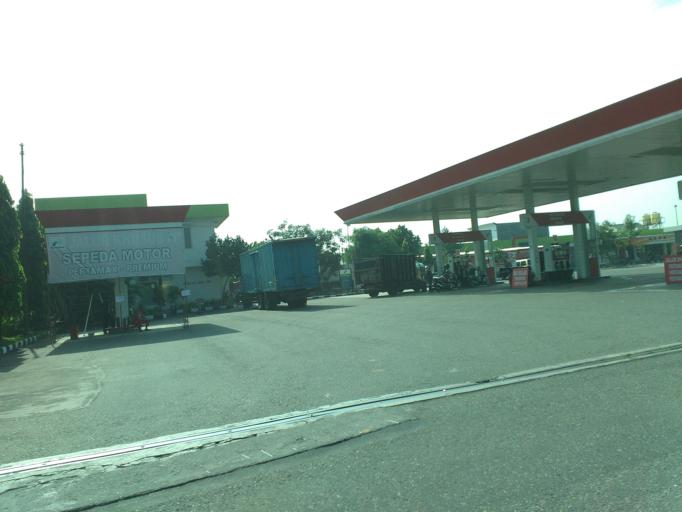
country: ID
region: Central Java
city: Delanggu
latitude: -7.6286
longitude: 110.6952
